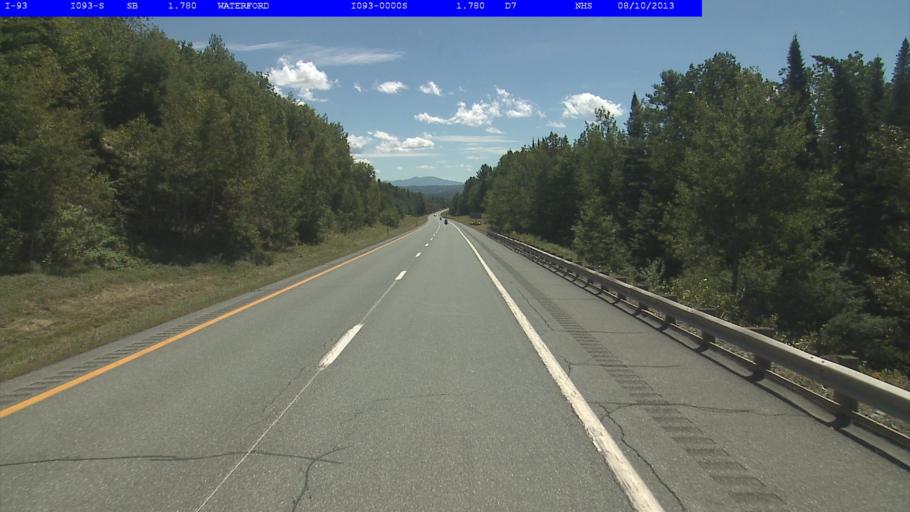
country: US
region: Vermont
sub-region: Caledonia County
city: Saint Johnsbury
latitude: 44.3673
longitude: -71.9039
